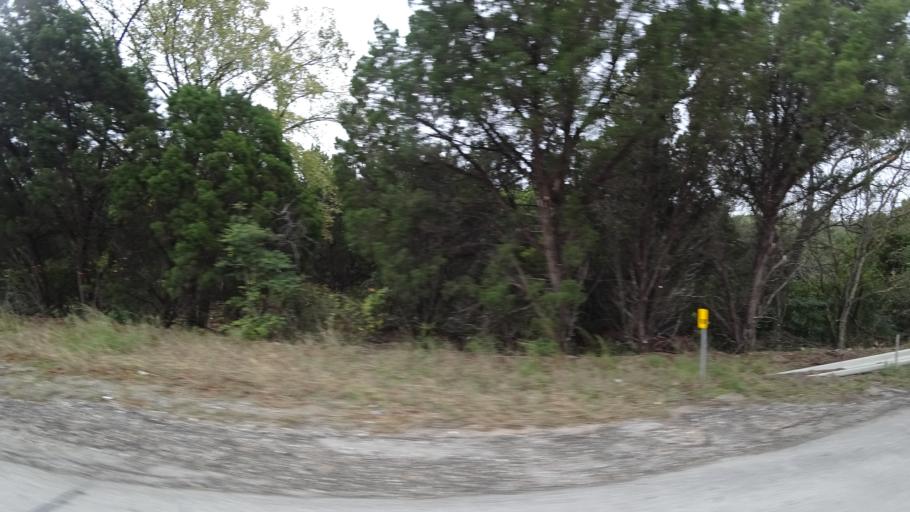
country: US
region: Texas
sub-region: Travis County
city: Barton Creek
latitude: 30.2319
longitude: -97.9008
